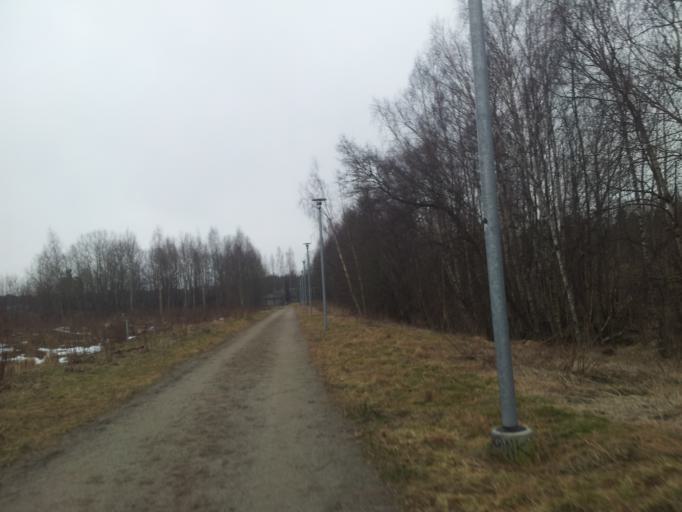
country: FI
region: Uusimaa
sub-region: Helsinki
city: Koukkuniemi
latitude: 60.1533
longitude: 24.7136
